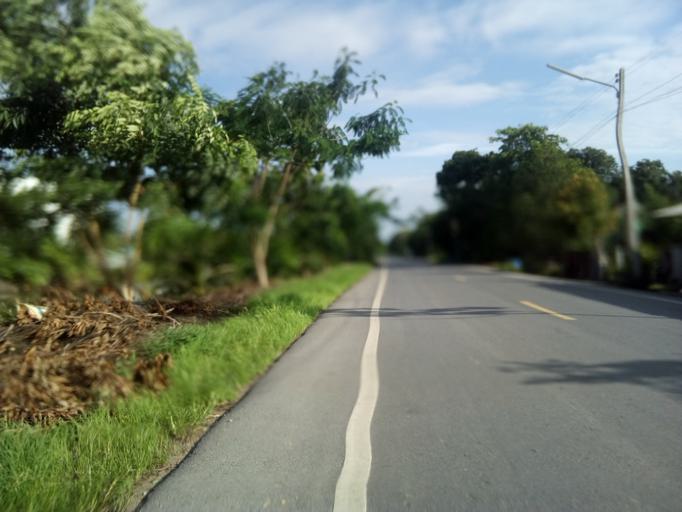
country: TH
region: Pathum Thani
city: Nong Suea
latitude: 14.0998
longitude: 100.8461
